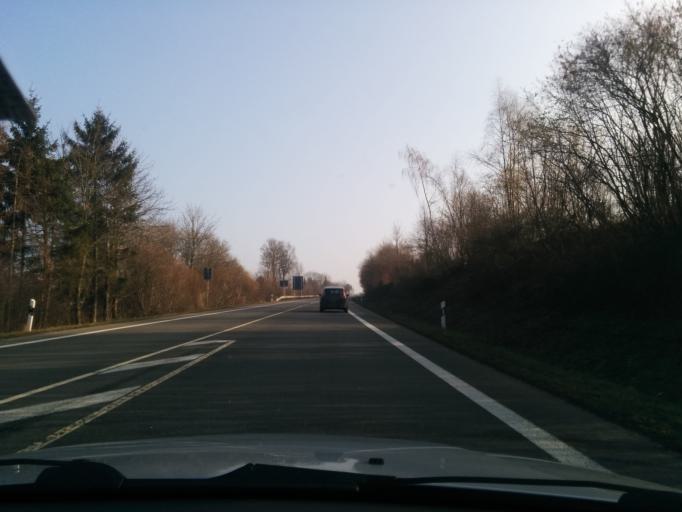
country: DE
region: North Rhine-Westphalia
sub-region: Regierungsbezirk Detmold
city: Nieheim
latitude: 51.8084
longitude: 9.1211
